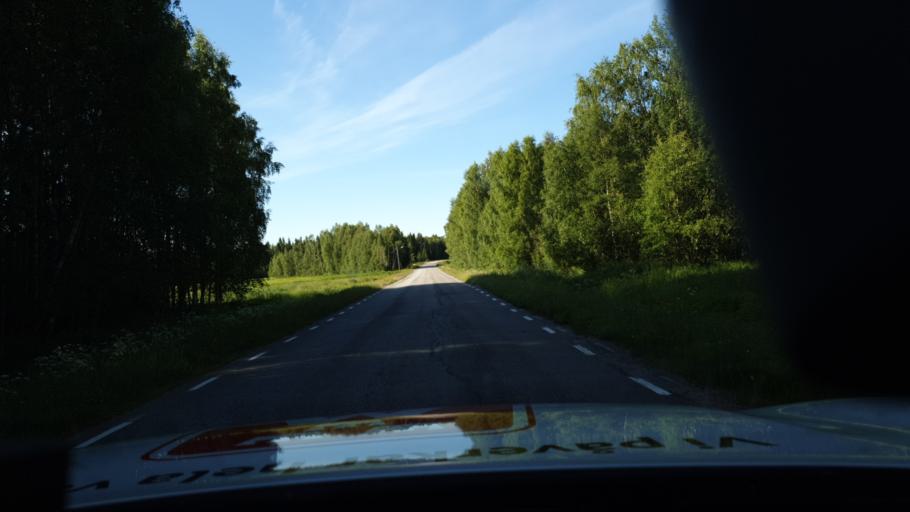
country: SE
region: Norrbotten
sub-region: Kalix Kommun
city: Toere
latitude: 65.8573
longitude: 22.6767
